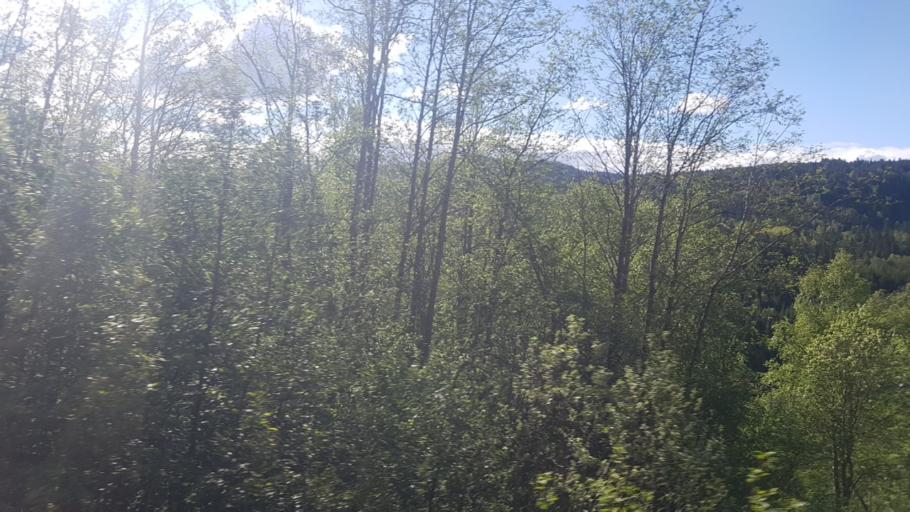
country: NO
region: Sor-Trondelag
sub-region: Midtre Gauldal
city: Storen
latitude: 62.9685
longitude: 10.2013
